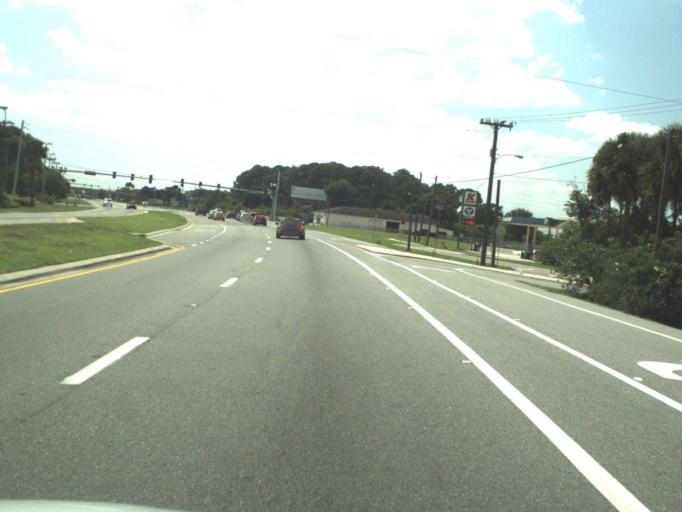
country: US
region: Florida
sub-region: Brevard County
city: Cocoa West
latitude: 28.3597
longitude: -80.7863
